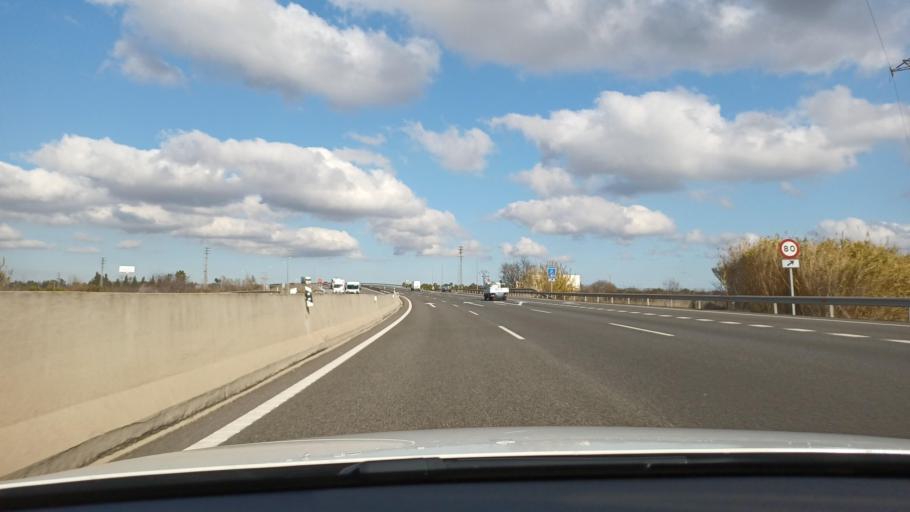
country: ES
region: Valencia
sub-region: Provincia de Valencia
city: L'Alcudia
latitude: 39.1897
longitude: -0.4985
